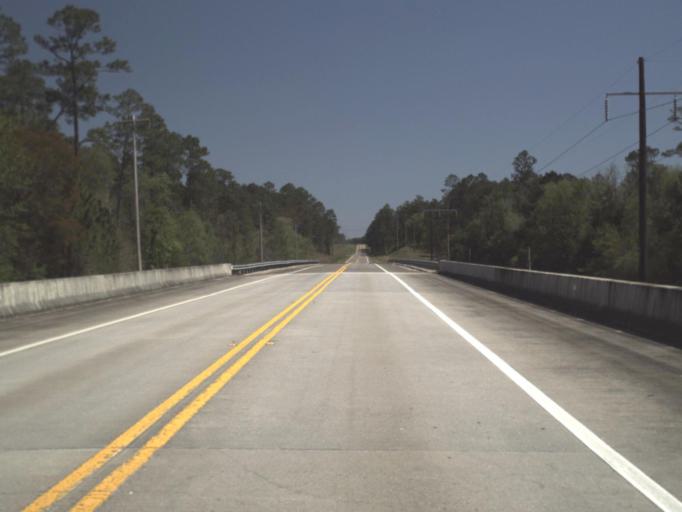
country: US
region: Florida
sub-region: Santa Rosa County
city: Point Baker
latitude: 30.8822
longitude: -86.9581
